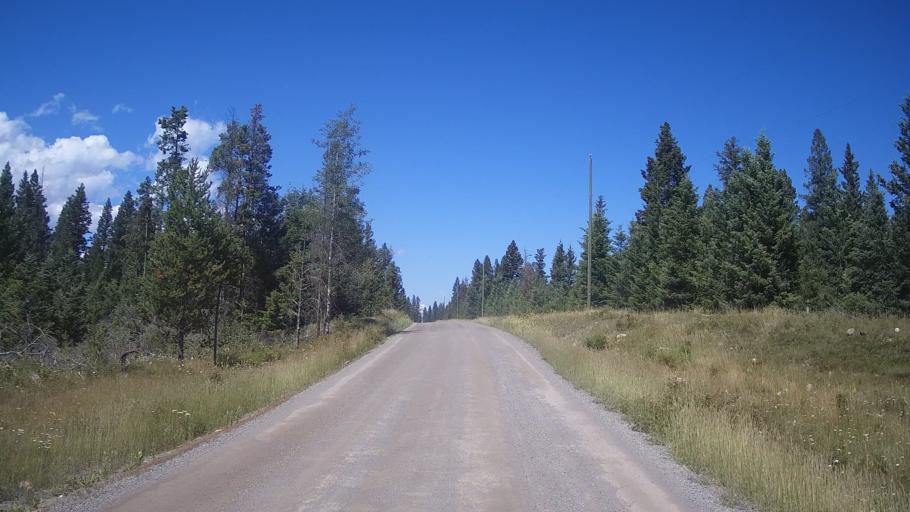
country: CA
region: British Columbia
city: Cache Creek
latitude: 51.2064
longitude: -121.5962
